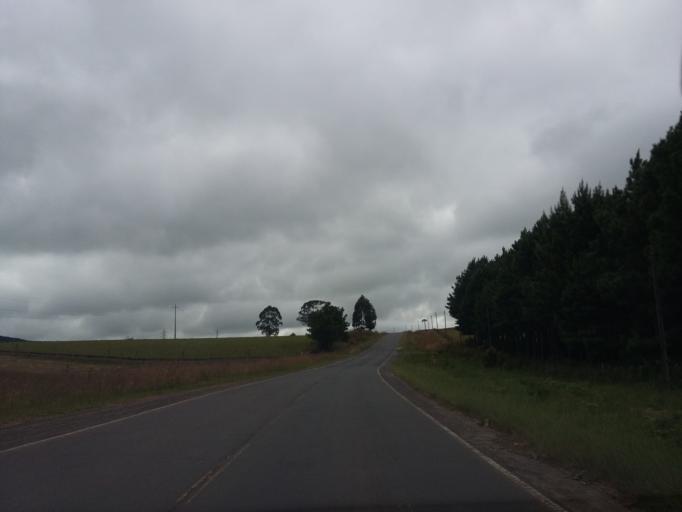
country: BR
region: Santa Catarina
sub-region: Lages
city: Lages
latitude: -27.8154
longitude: -50.2757
